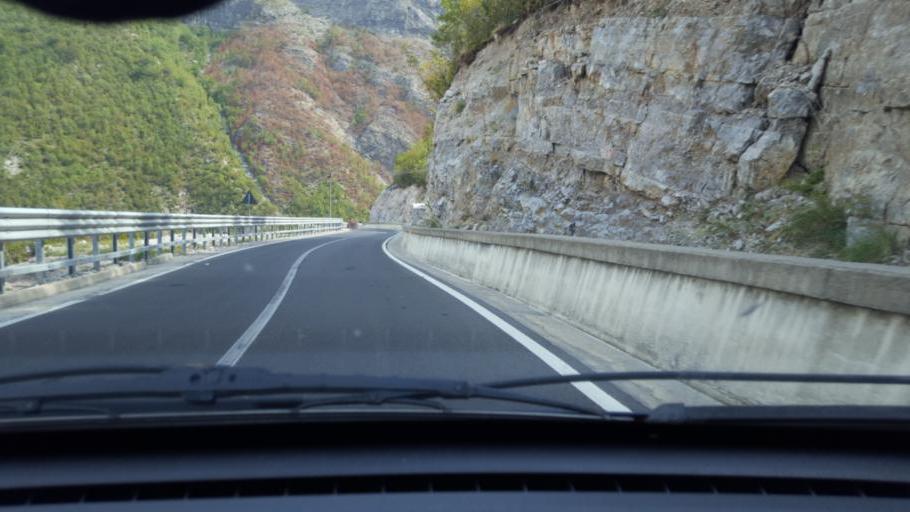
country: AL
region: Shkoder
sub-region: Rrethi i Malesia e Madhe
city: Kastrat
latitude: 42.4157
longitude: 19.5072
